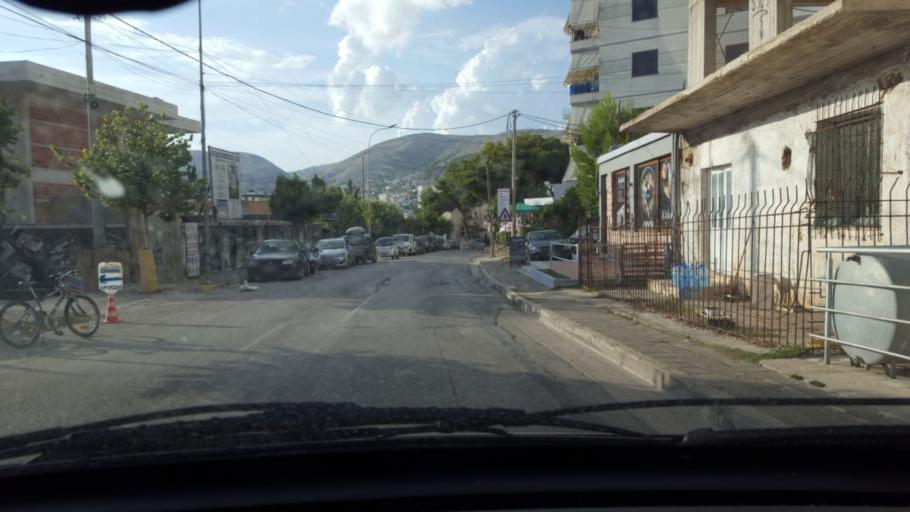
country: AL
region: Vlore
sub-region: Rrethi i Sarandes
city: Sarande
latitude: 39.8648
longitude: 20.0167
